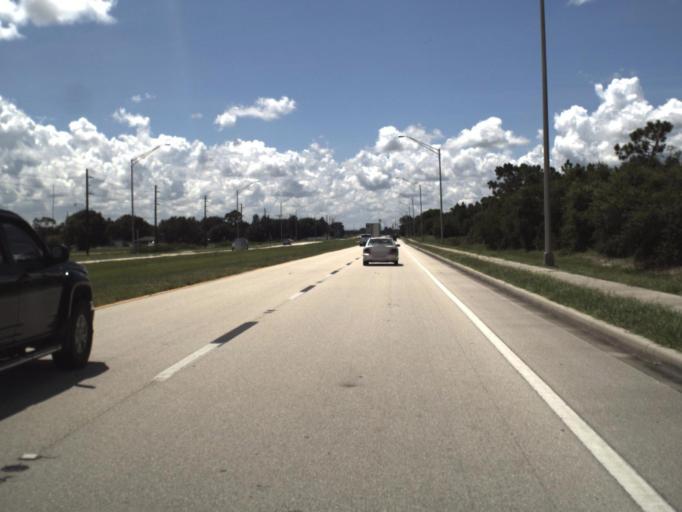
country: US
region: Florida
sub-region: Charlotte County
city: Cleveland
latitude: 26.9921
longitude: -81.9592
